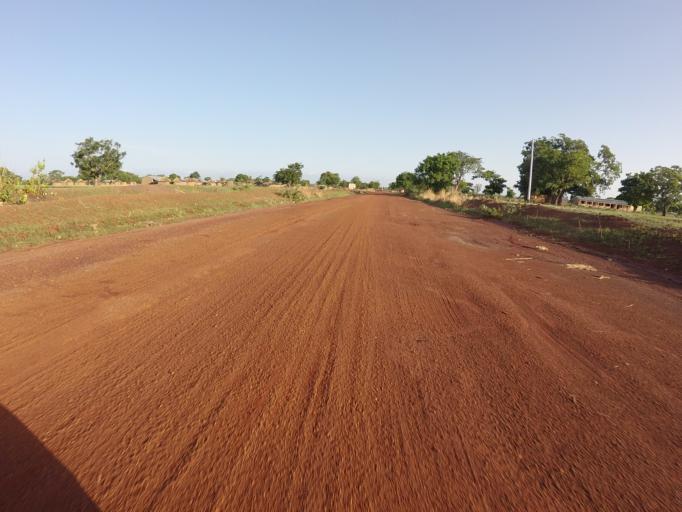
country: TG
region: Savanes
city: Sansanne-Mango
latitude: 10.3589
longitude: -0.0934
